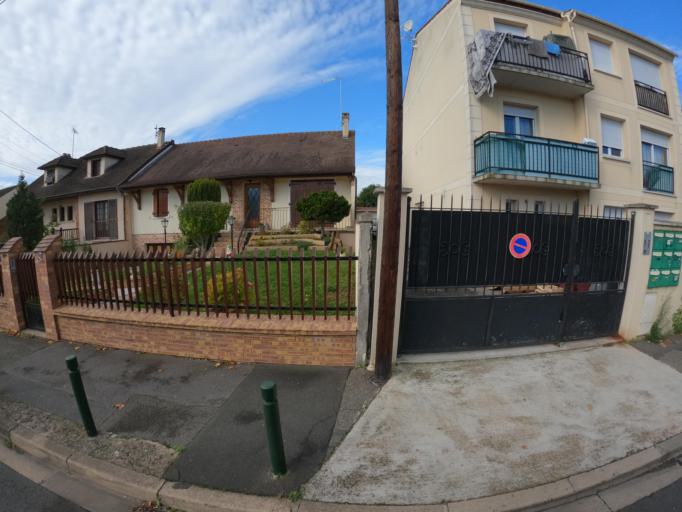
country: FR
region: Ile-de-France
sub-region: Departement de Seine-et-Marne
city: Brou-sur-Chantereine
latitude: 48.8799
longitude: 2.6188
